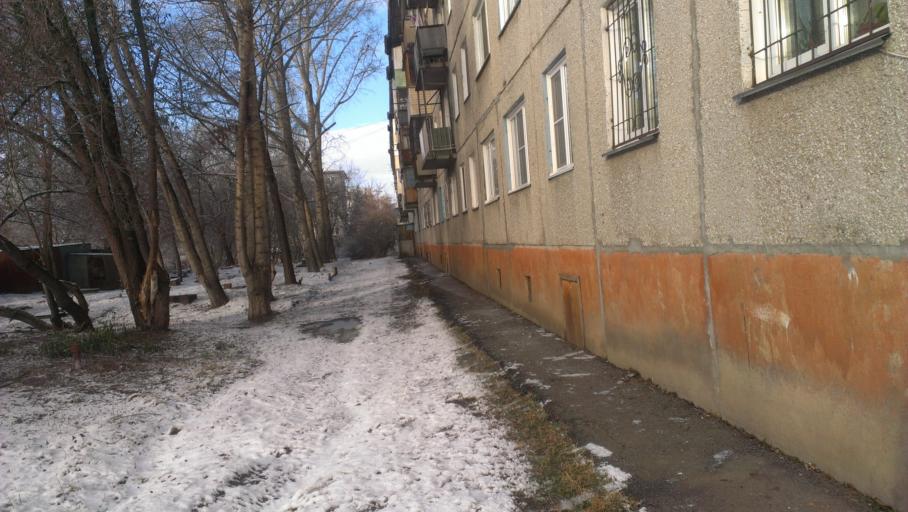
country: RU
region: Altai Krai
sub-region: Gorod Barnaulskiy
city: Barnaul
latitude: 53.3645
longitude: 83.6898
